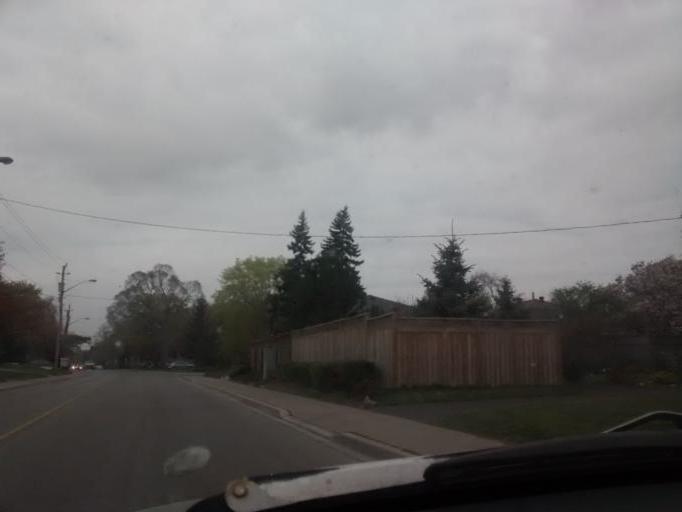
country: CA
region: Ontario
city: Burlington
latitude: 43.3368
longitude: -79.7959
